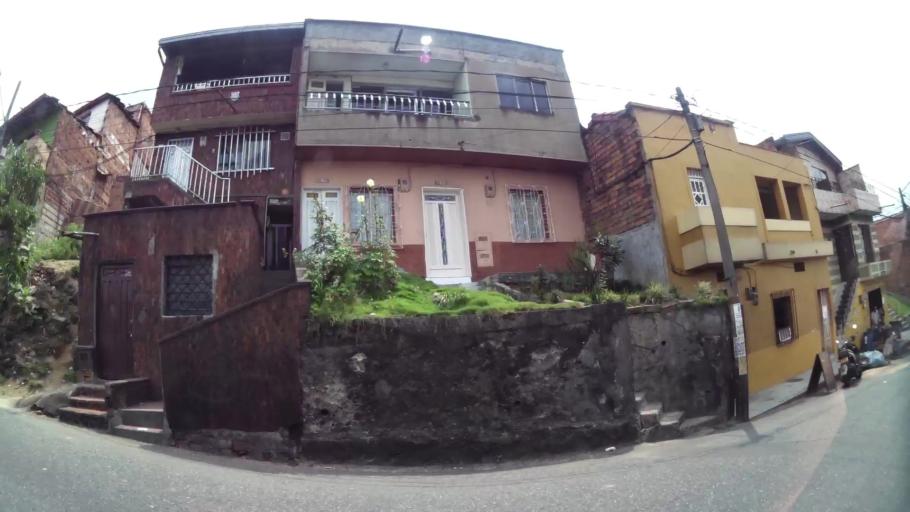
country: CO
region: Antioquia
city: Medellin
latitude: 6.2635
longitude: -75.5487
